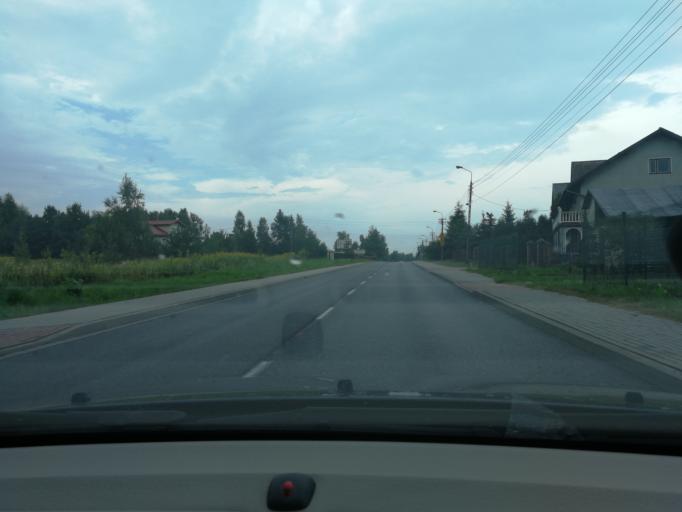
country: PL
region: Masovian Voivodeship
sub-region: Powiat zyrardowski
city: Radziejowice
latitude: 52.0069
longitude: 20.5571
